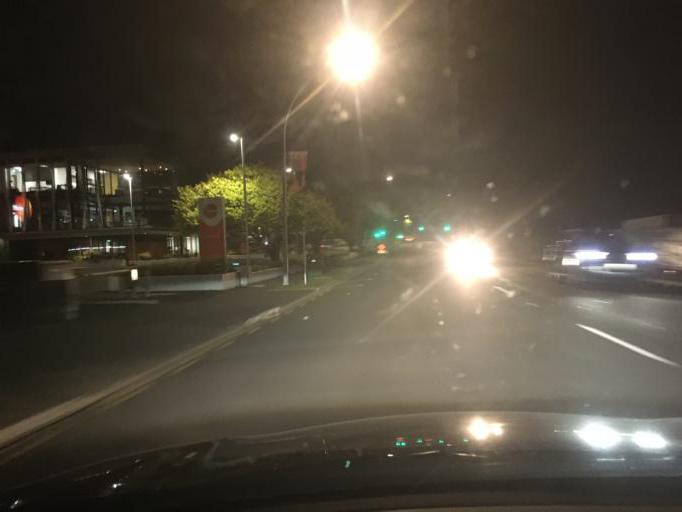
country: NZ
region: Waikato
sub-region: Hamilton City
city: Hamilton
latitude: -37.7866
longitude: 175.2756
